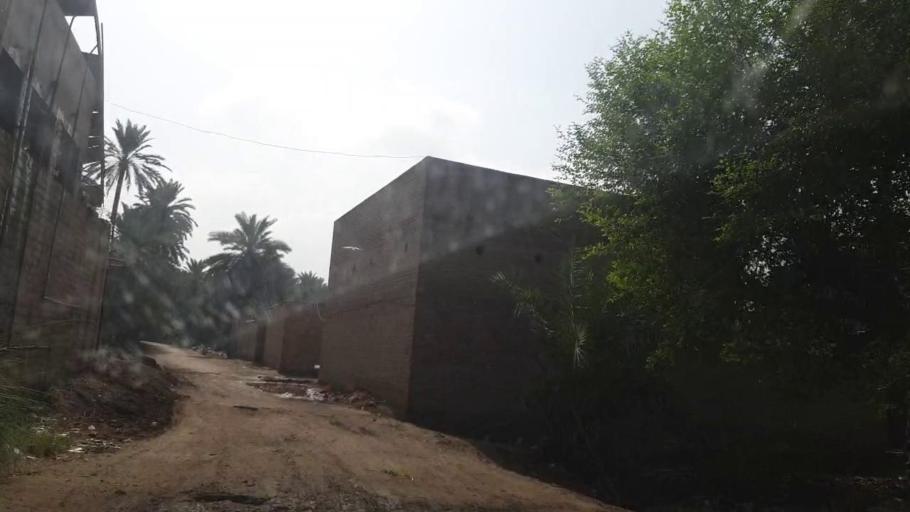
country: PK
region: Sindh
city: Khairpur
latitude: 27.5704
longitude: 68.7489
